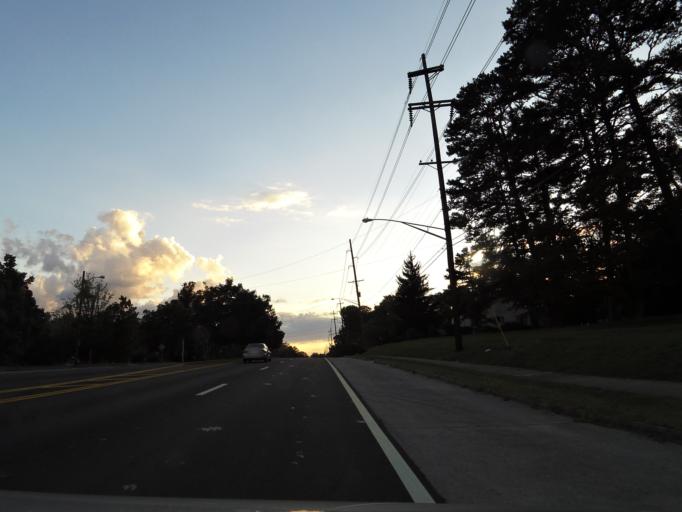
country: US
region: Tennessee
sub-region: Knox County
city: Knoxville
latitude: 36.0089
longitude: -83.8456
